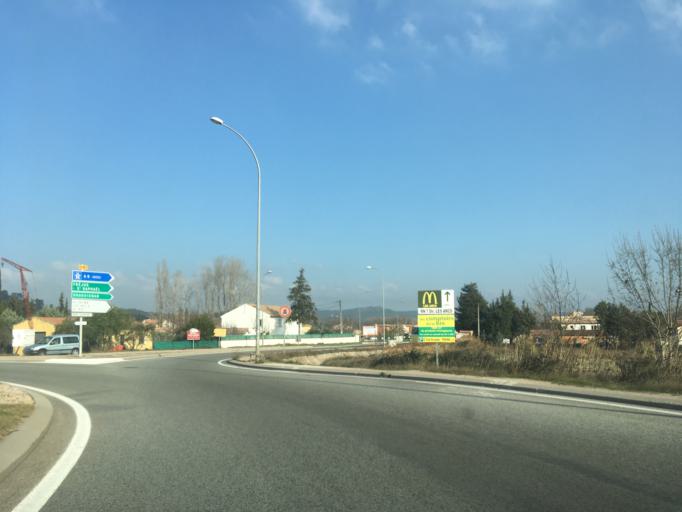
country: FR
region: Provence-Alpes-Cote d'Azur
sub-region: Departement du Var
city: Vidauban
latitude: 43.4143
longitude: 6.4193
